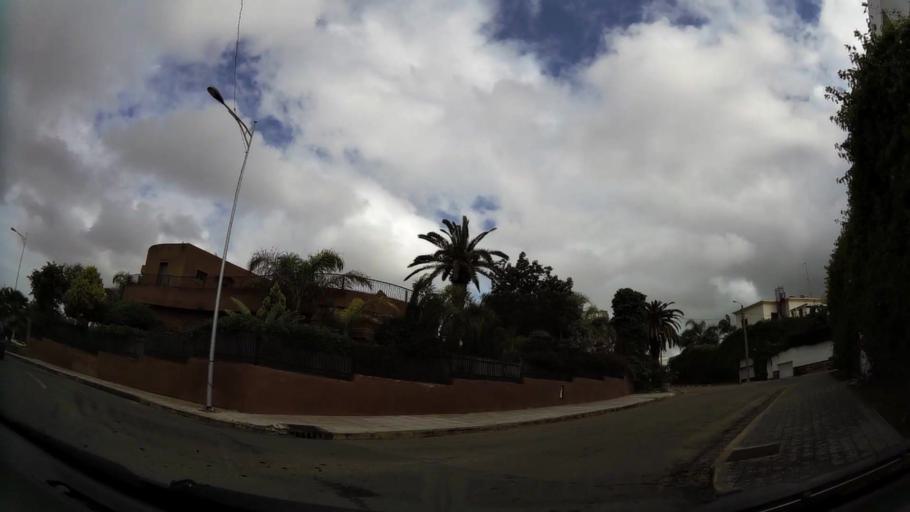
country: MA
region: Grand Casablanca
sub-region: Casablanca
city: Casablanca
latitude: 33.5520
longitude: -7.6190
